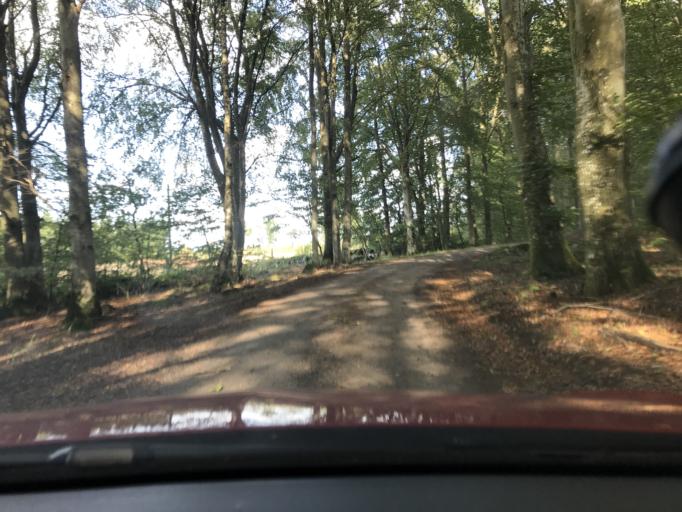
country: SE
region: Skane
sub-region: Hassleholms Kommun
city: Sosdala
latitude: 56.0048
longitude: 13.7059
